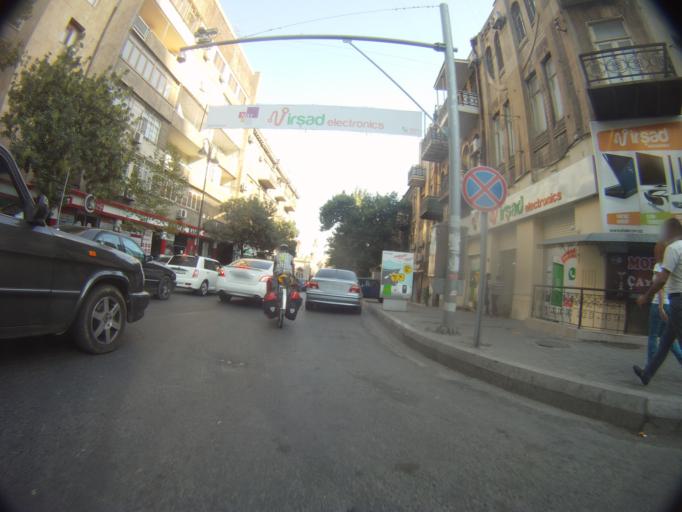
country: AZ
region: Baki
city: Baku
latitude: 40.3778
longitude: 49.8480
